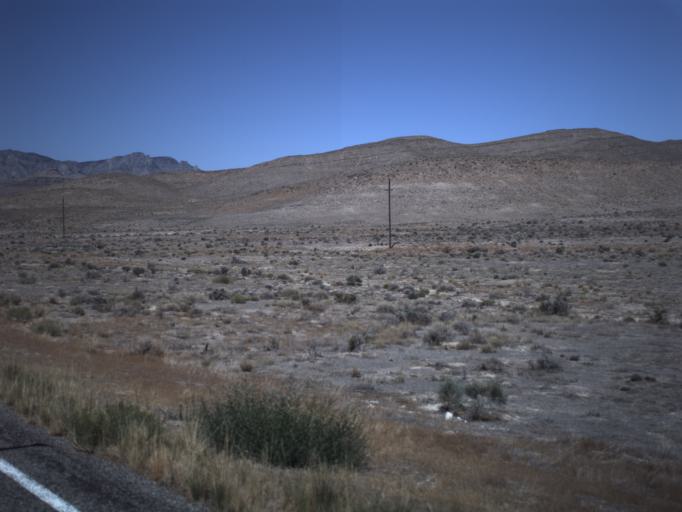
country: US
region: Utah
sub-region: Beaver County
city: Milford
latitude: 39.0254
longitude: -113.3533
